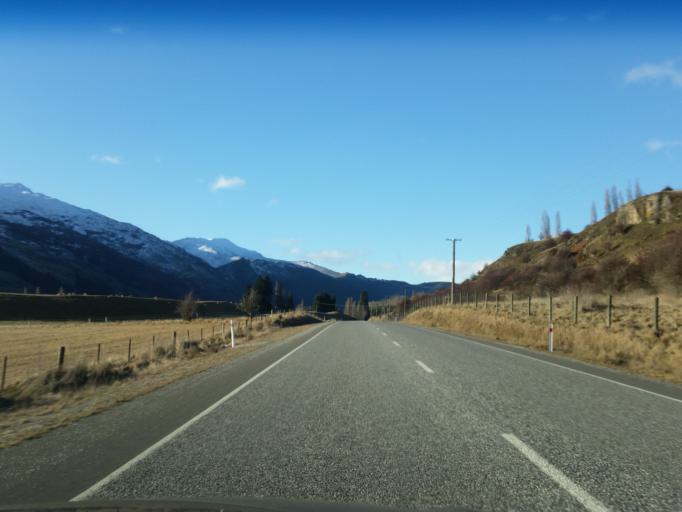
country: NZ
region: Otago
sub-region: Queenstown-Lakes District
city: Queenstown
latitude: -44.9639
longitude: 168.7160
